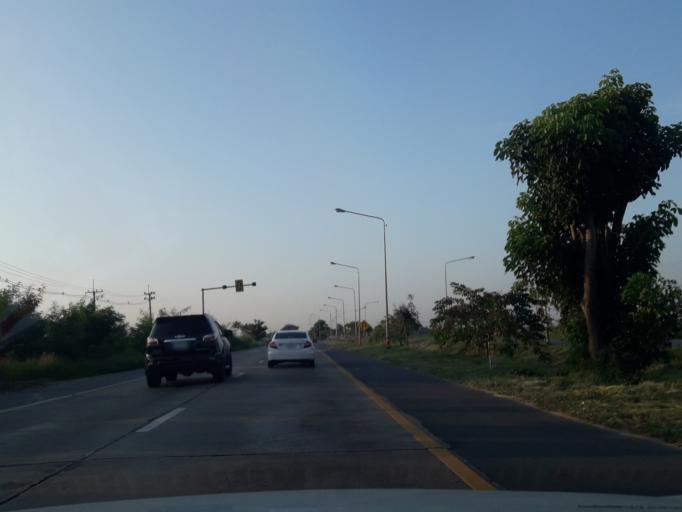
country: TH
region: Phra Nakhon Si Ayutthaya
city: Phra Nakhon Si Ayutthaya
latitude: 14.3031
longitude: 100.5256
